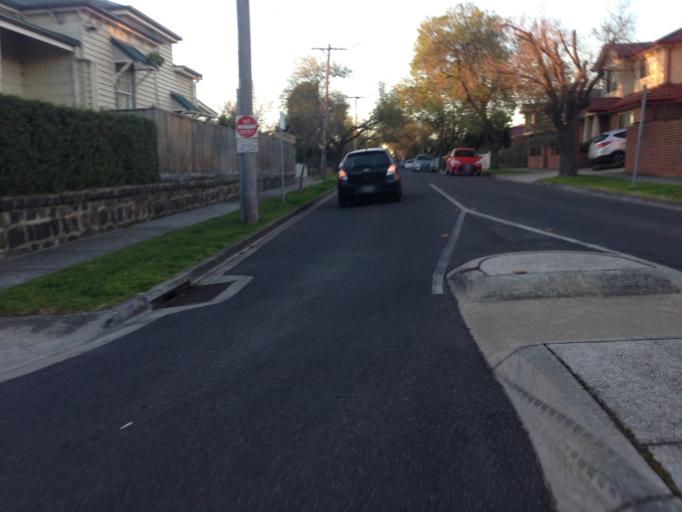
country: AU
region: Victoria
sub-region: Darebin
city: Fairfield
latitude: -37.7737
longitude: 145.0134
